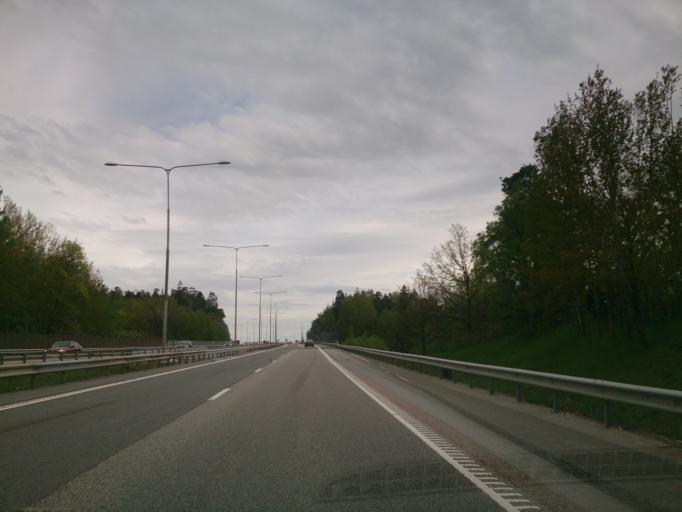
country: SE
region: Stockholm
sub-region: Nacka Kommun
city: Alta
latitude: 59.2362
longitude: 18.1227
